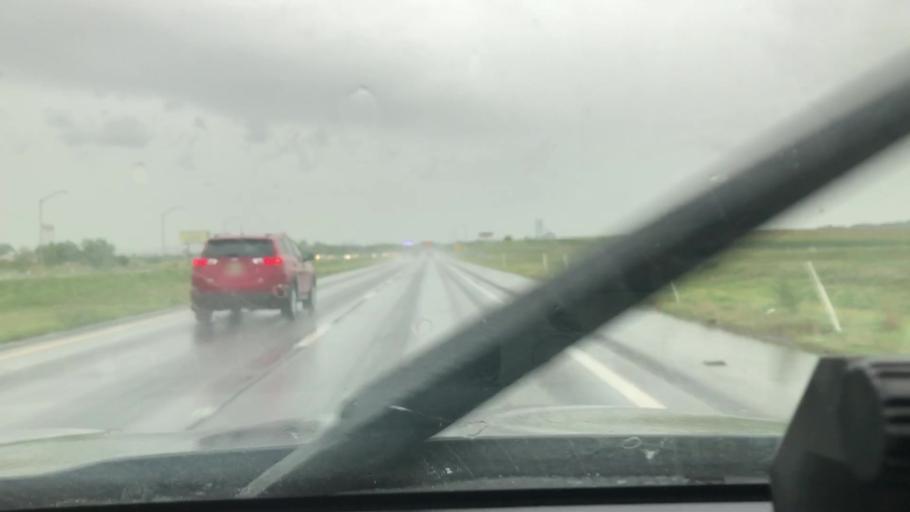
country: US
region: Pennsylvania
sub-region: Northampton County
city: Tatamy
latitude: 40.7380
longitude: -75.2681
